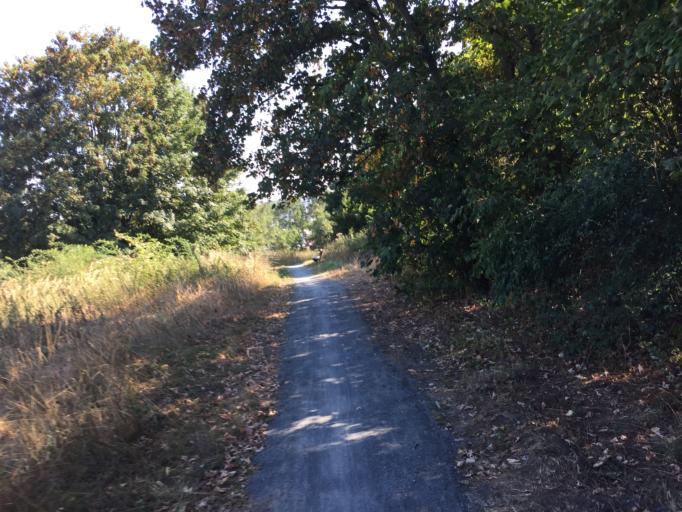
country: DE
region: Hesse
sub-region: Regierungsbezirk Giessen
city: Hoernsheim
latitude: 50.5432
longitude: 8.6544
